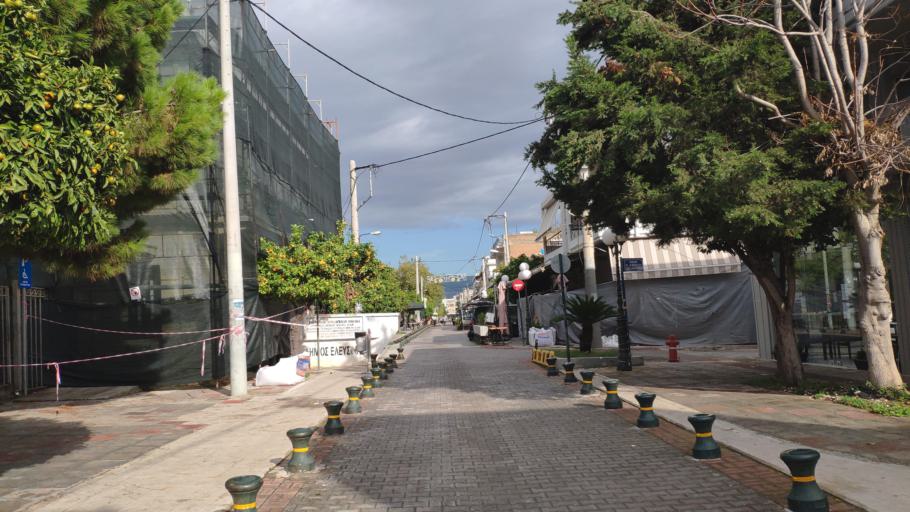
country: GR
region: Attica
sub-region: Nomarchia Dytikis Attikis
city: Elefsina
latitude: 38.0413
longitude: 23.5400
